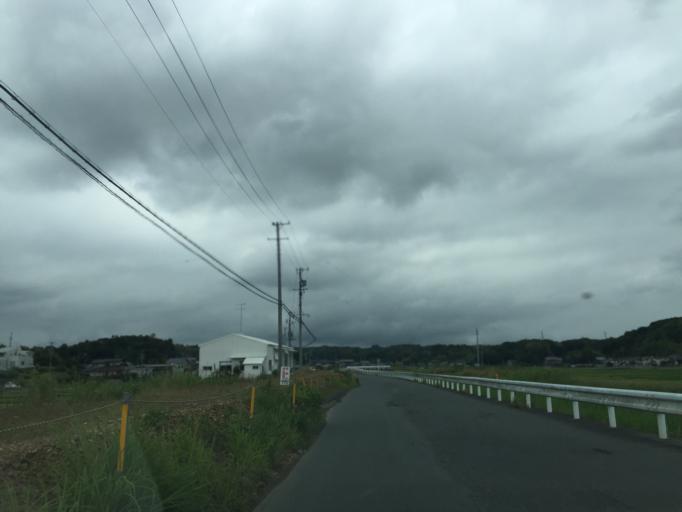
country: JP
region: Shizuoka
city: Fukuroi
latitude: 34.7648
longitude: 137.9366
